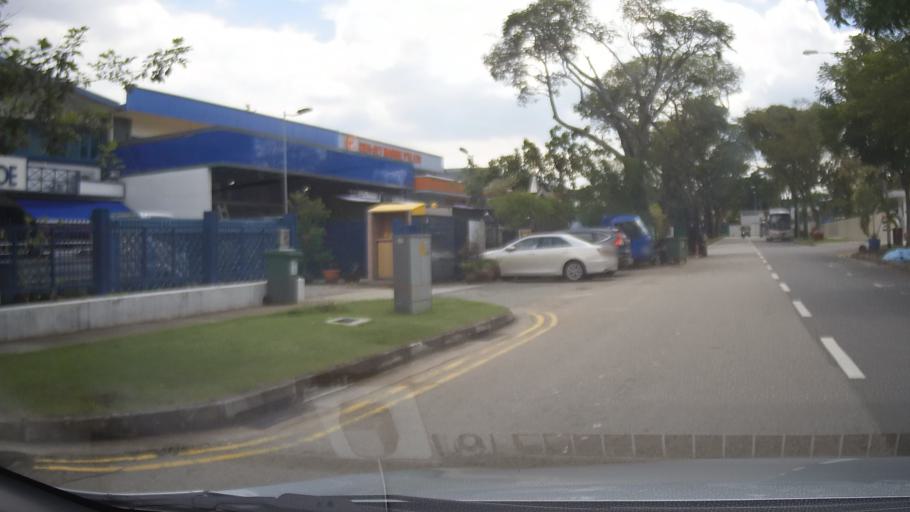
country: MY
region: Johor
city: Johor Bahru
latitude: 1.3263
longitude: 103.6917
